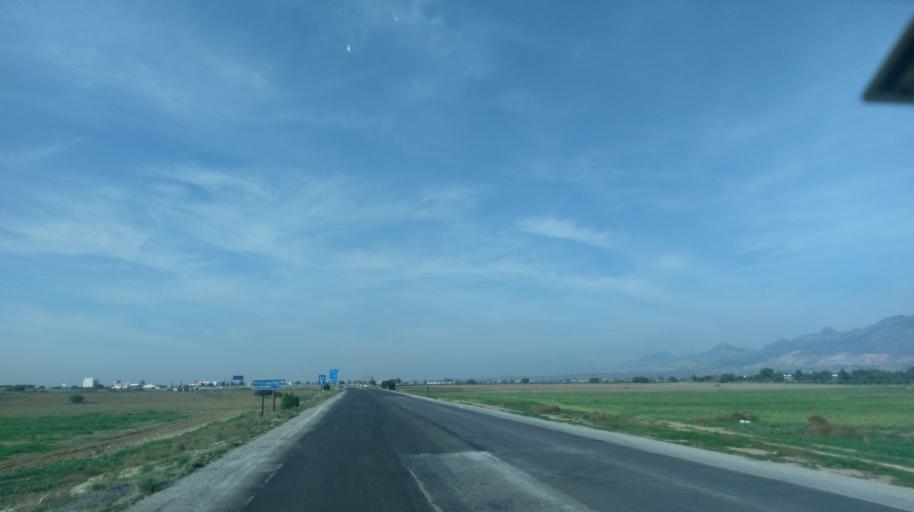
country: CY
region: Lefkosia
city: Geri
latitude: 35.2221
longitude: 33.5053
